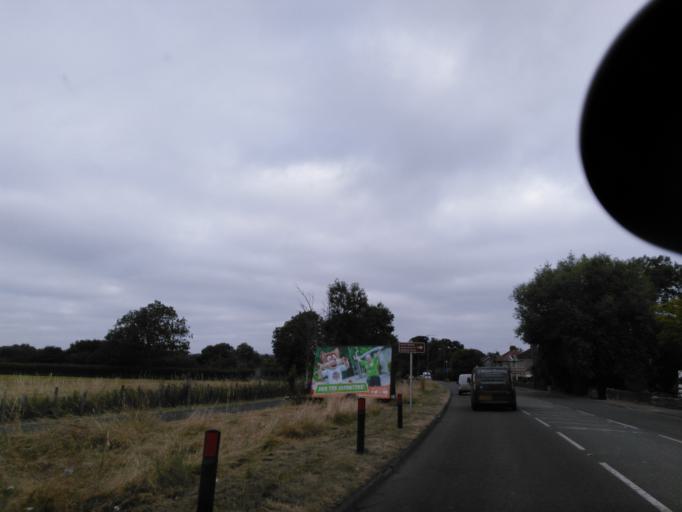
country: GB
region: England
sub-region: Bath and North East Somerset
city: Saltford
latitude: 51.4100
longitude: -2.4749
